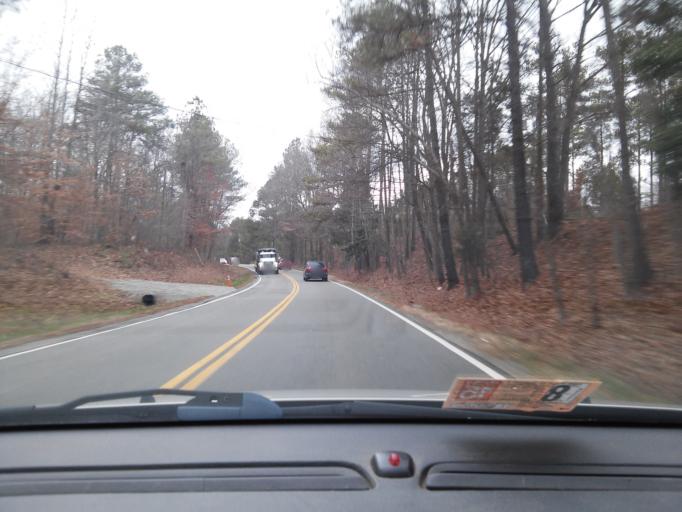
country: US
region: Virginia
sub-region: Henrico County
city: Short Pump
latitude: 37.5574
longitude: -77.6764
